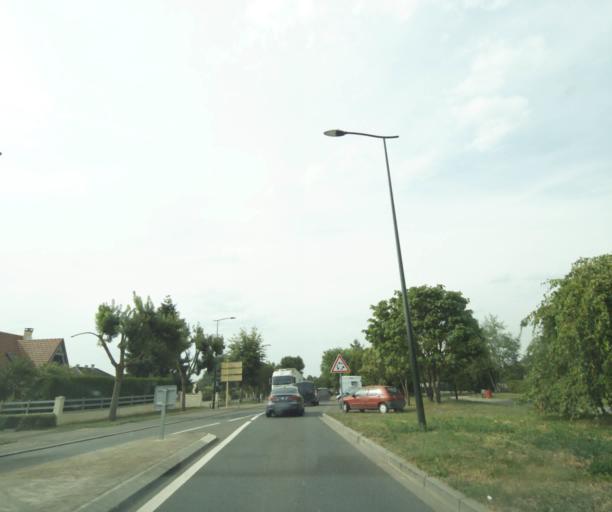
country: FR
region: Pays de la Loire
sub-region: Departement de la Sarthe
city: Mulsanne
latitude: 47.9071
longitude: 0.2446
